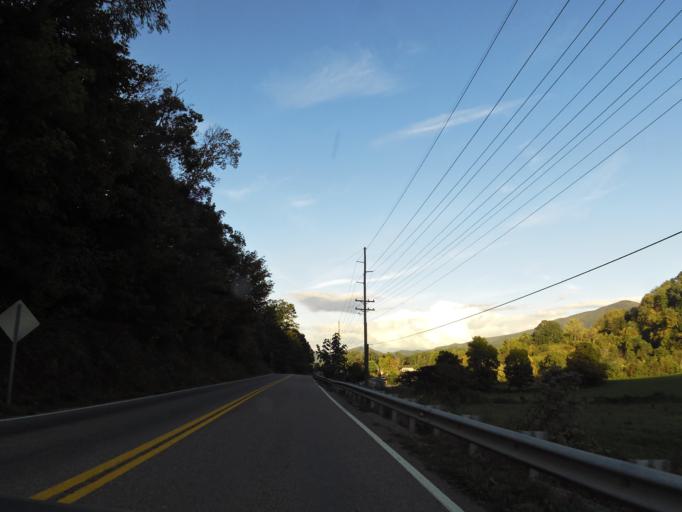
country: US
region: Tennessee
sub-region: Sevier County
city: Pigeon Forge
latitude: 35.7013
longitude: -83.6774
